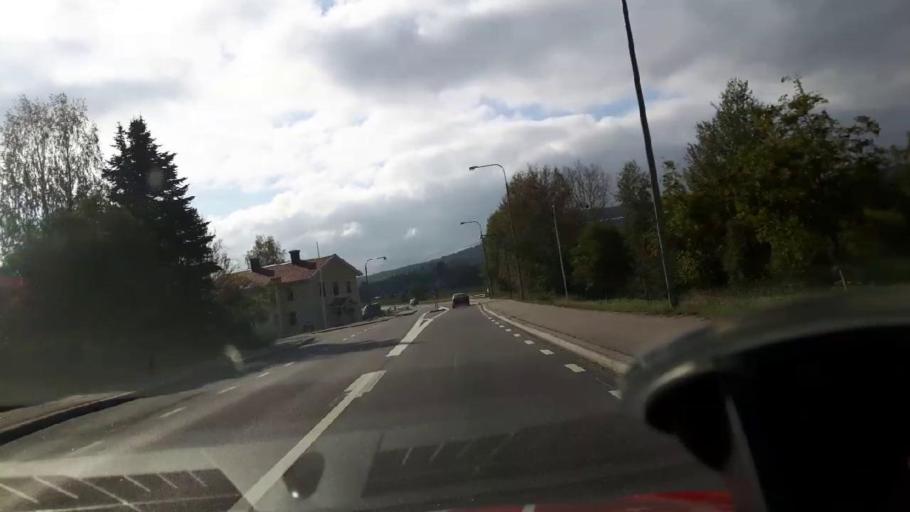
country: SE
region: Gaevleborg
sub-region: Bollnas Kommun
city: Arbra
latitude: 61.5143
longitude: 16.3615
